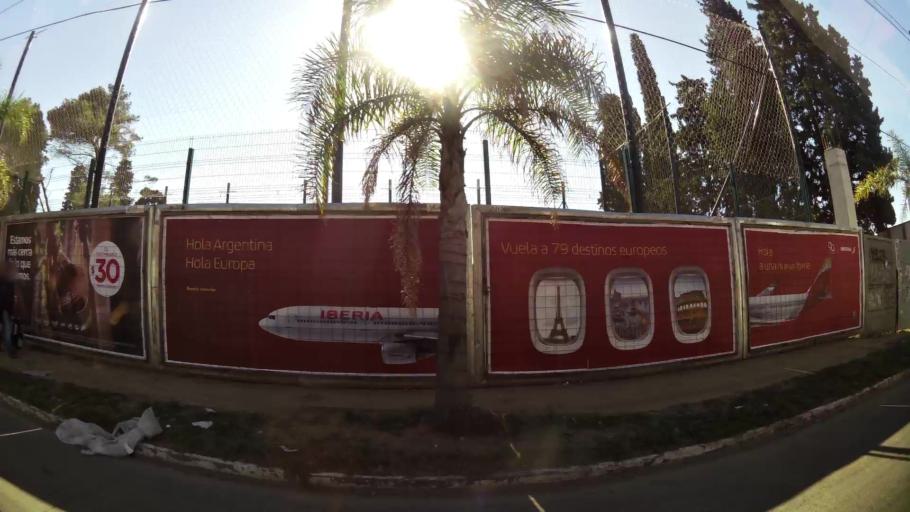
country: AR
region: Buenos Aires
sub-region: Partido de Lomas de Zamora
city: Lomas de Zamora
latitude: -34.7705
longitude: -58.4236
